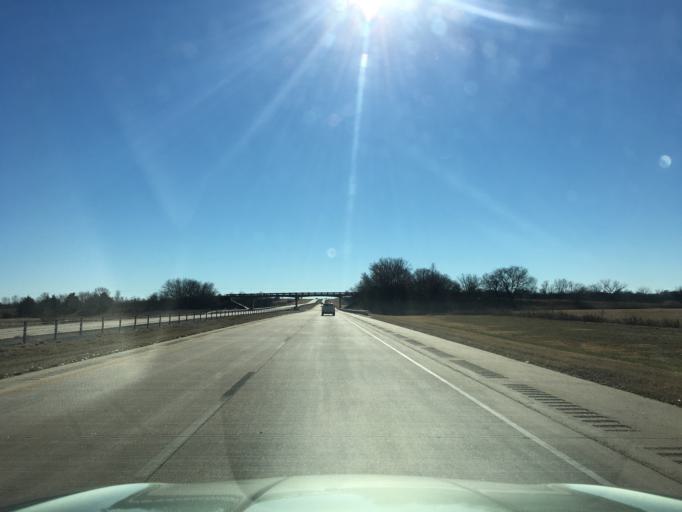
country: US
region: Oklahoma
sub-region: Noble County
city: Perry
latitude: 36.4658
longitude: -97.3271
